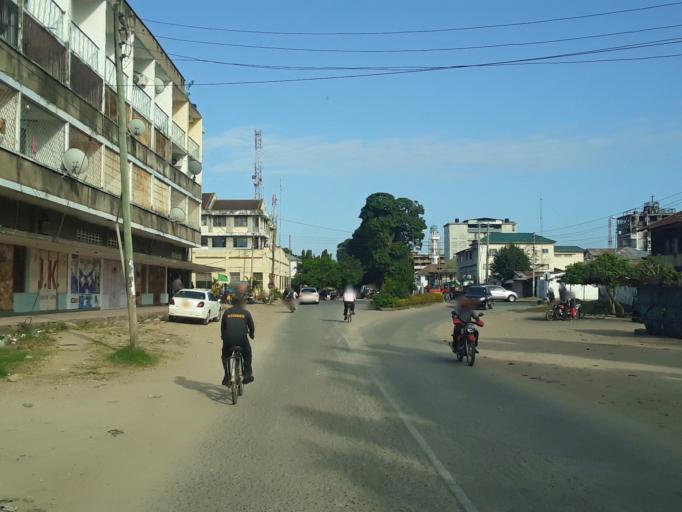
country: TZ
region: Tanga
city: Tanga
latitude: -5.0728
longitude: 39.1070
